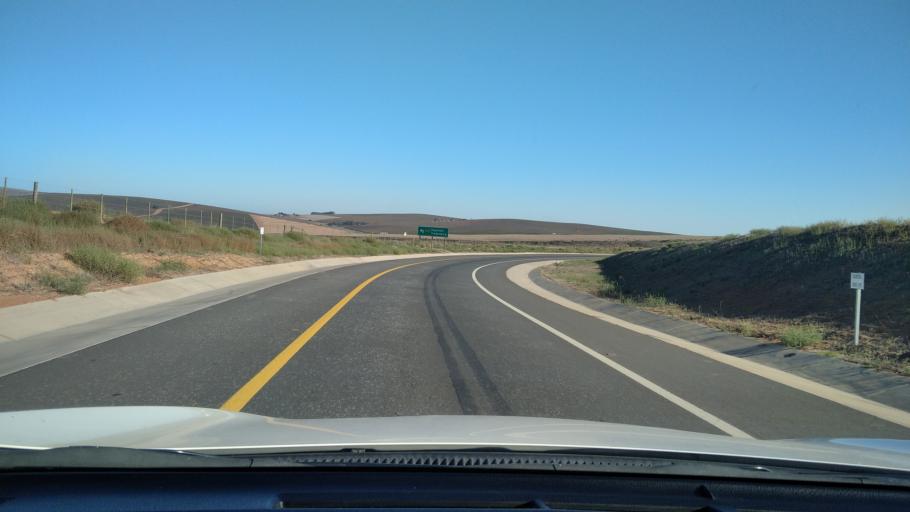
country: ZA
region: Western Cape
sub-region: West Coast District Municipality
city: Malmesbury
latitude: -33.4159
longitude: 18.7117
